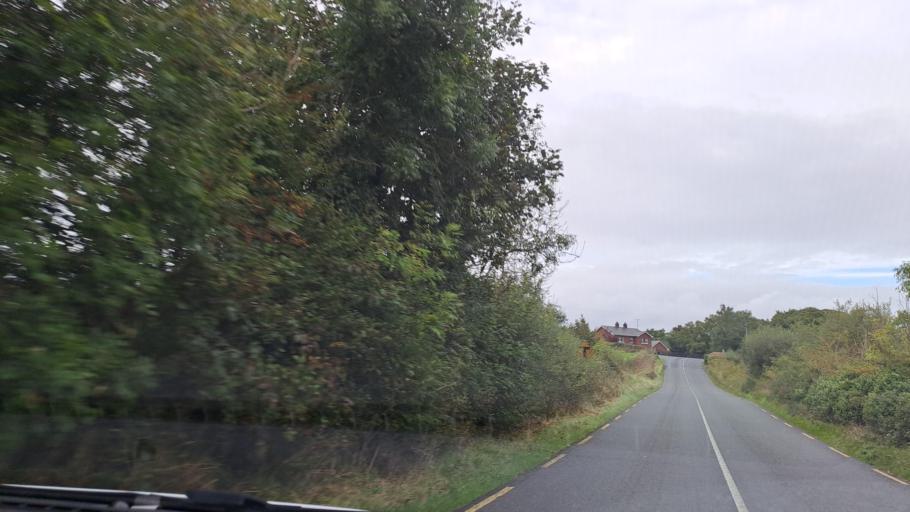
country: IE
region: Ulster
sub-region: An Cabhan
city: Bailieborough
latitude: 54.0364
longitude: -6.8958
